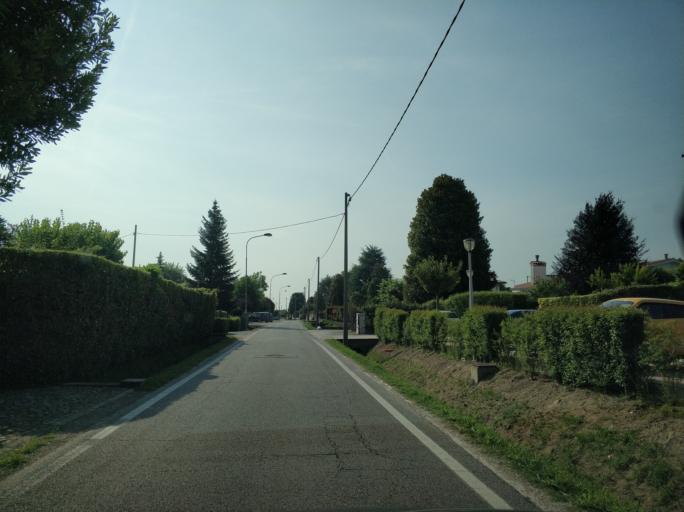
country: IT
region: Veneto
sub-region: Provincia di Padova
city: Este
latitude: 45.2260
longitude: 11.6669
